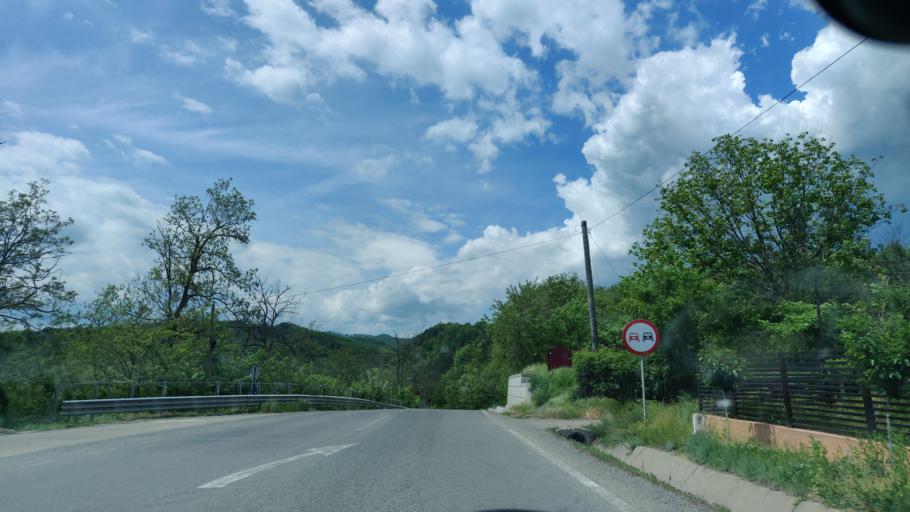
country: RO
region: Vrancea
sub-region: Comuna Vidra
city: Vidra
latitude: 45.8968
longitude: 26.8565
